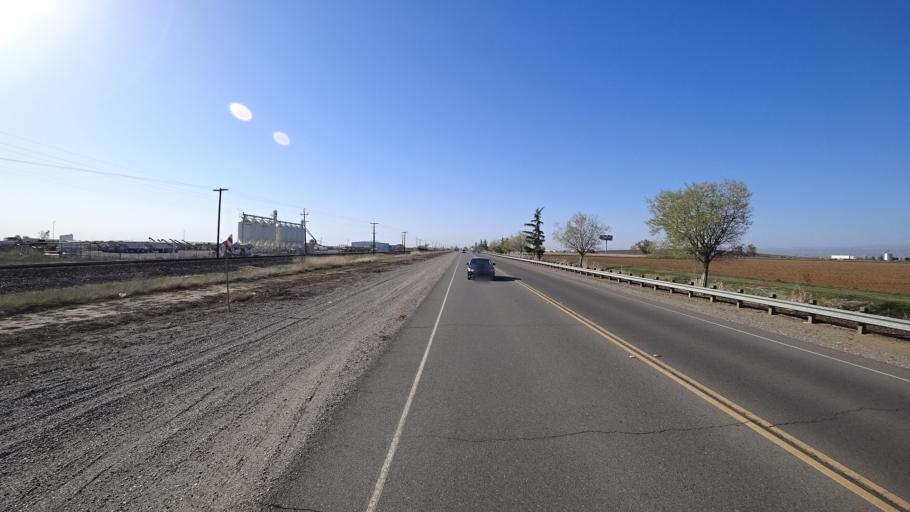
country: US
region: California
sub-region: Glenn County
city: Willows
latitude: 39.4991
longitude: -122.1932
